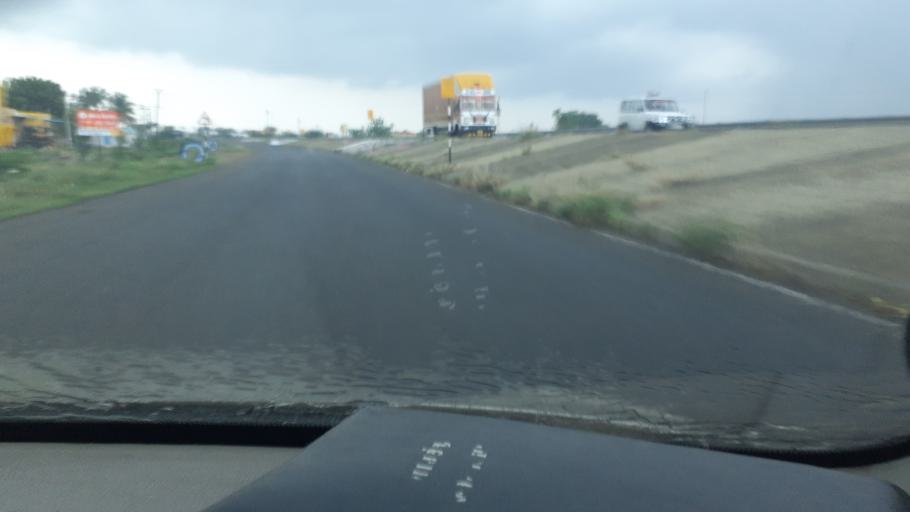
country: IN
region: Tamil Nadu
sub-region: Thoothukkudi
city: Kovilpatti
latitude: 9.0991
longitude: 77.8070
